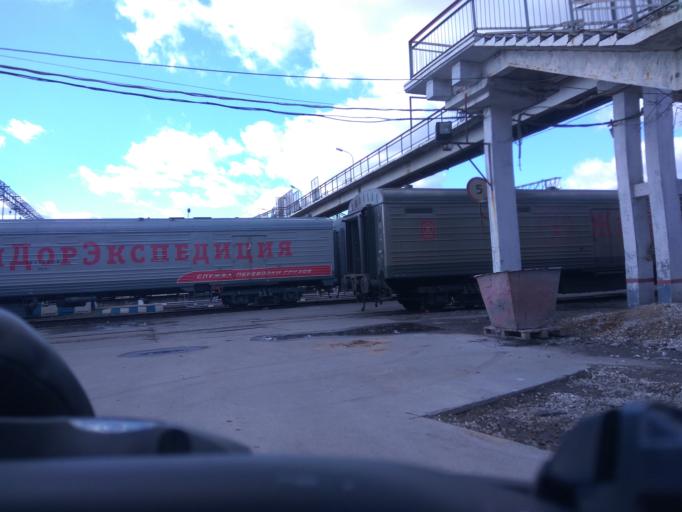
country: RU
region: Moscow
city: Sokol'niki
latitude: 55.8020
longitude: 37.6528
